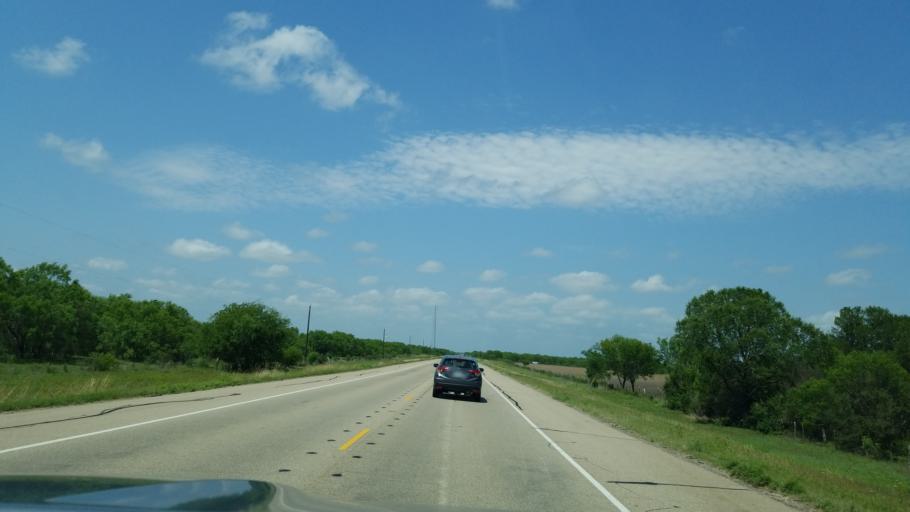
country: US
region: Texas
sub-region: Frio County
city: Pearsall
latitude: 29.0132
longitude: -99.1215
